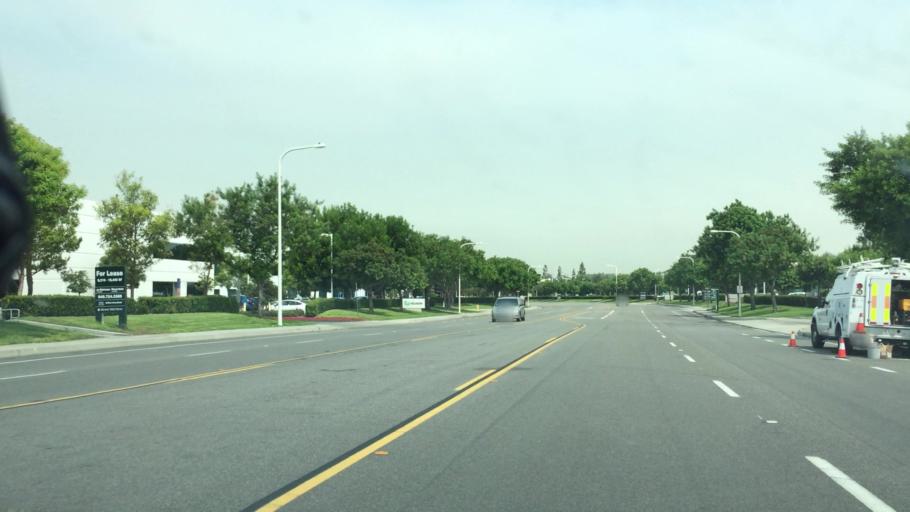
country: US
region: California
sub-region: Orange County
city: Laguna Woods
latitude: 33.6410
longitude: -117.7371
